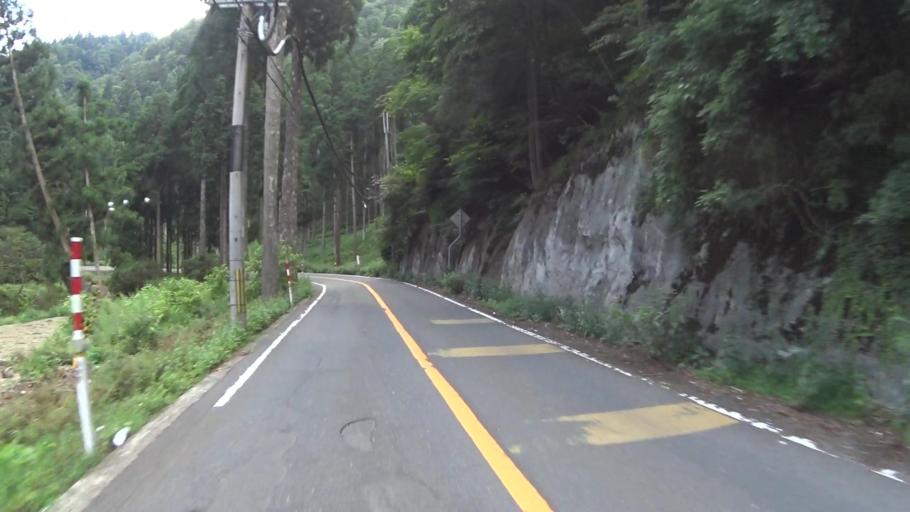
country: JP
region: Kyoto
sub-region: Kyoto-shi
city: Kamigyo-ku
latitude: 35.2403
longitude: 135.6534
